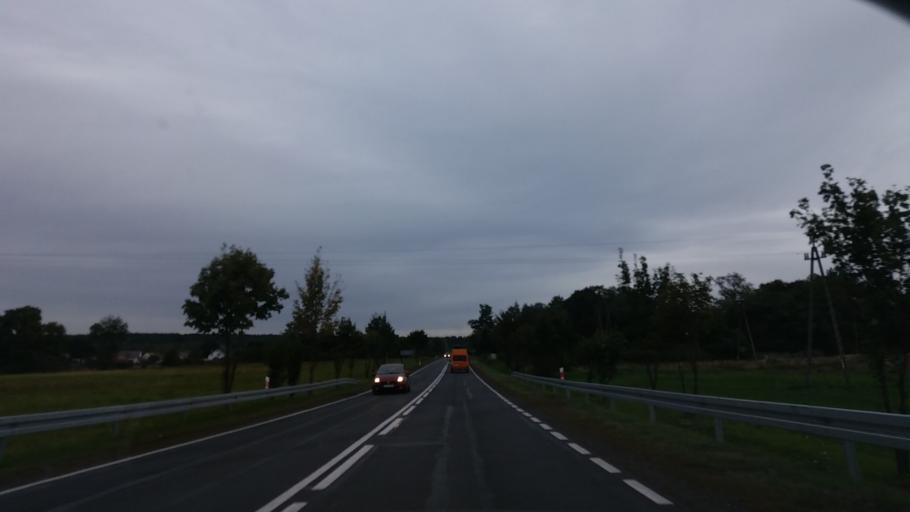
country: PL
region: Lower Silesian Voivodeship
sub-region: Powiat legnicki
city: Prochowice
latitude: 51.2828
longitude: 16.3476
